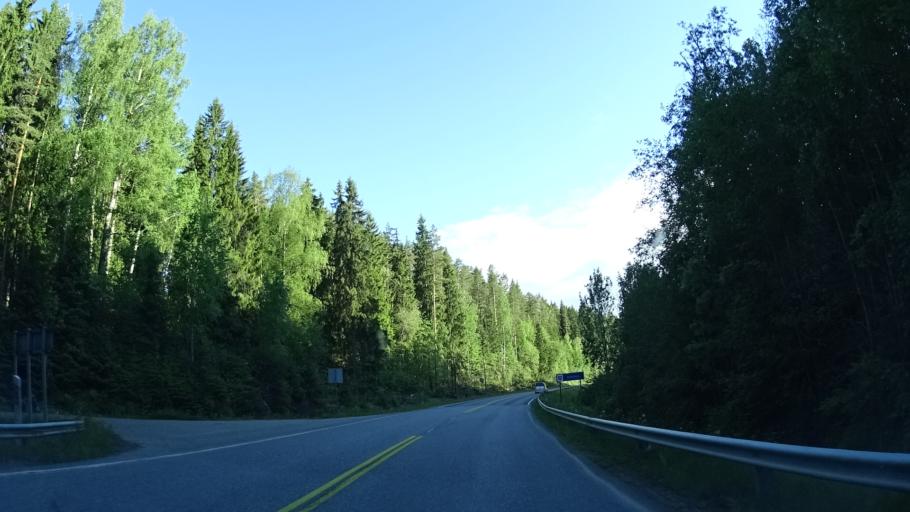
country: FI
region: Paijanne Tavastia
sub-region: Lahti
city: Asikkala
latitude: 61.3417
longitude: 25.5945
